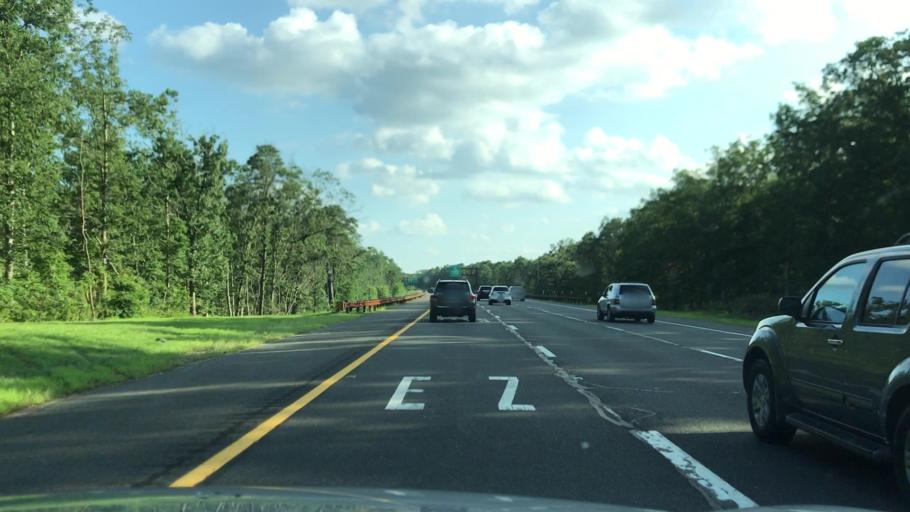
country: US
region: New Jersey
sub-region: Ocean County
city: Barnegat
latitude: 39.7878
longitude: -74.2412
